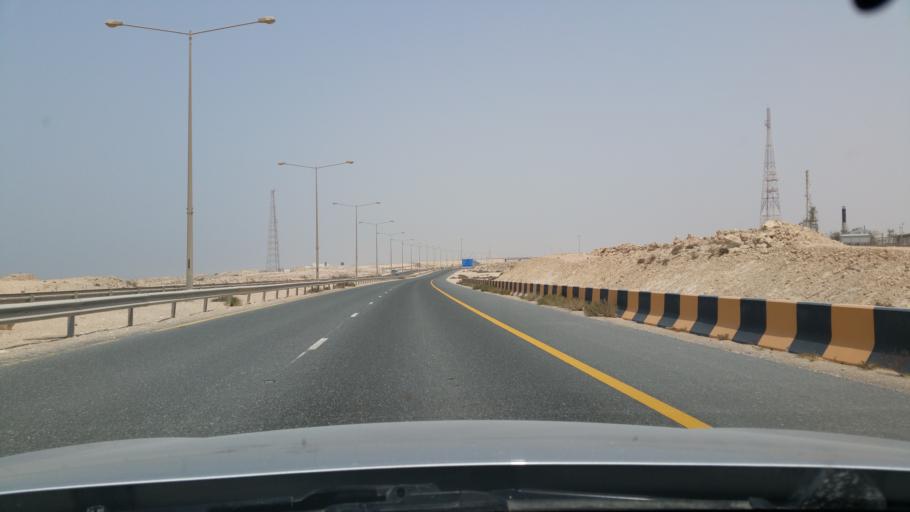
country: QA
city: Umm Bab
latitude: 25.2845
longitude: 50.7909
